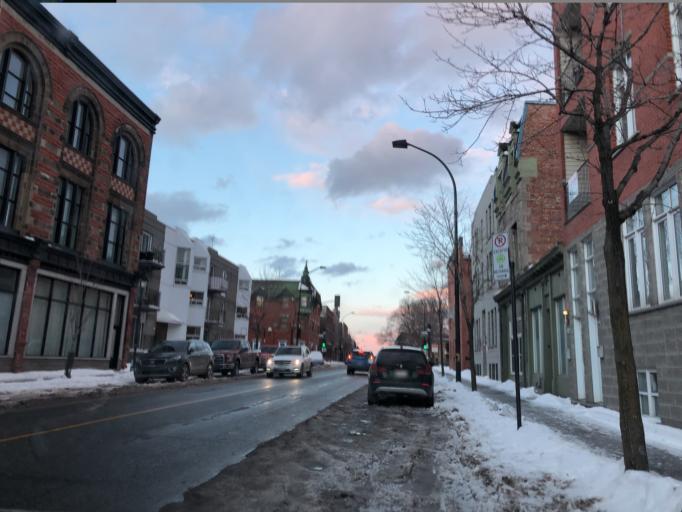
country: CA
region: Quebec
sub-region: Monteregie
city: Longueuil
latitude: 45.5386
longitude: -73.5416
